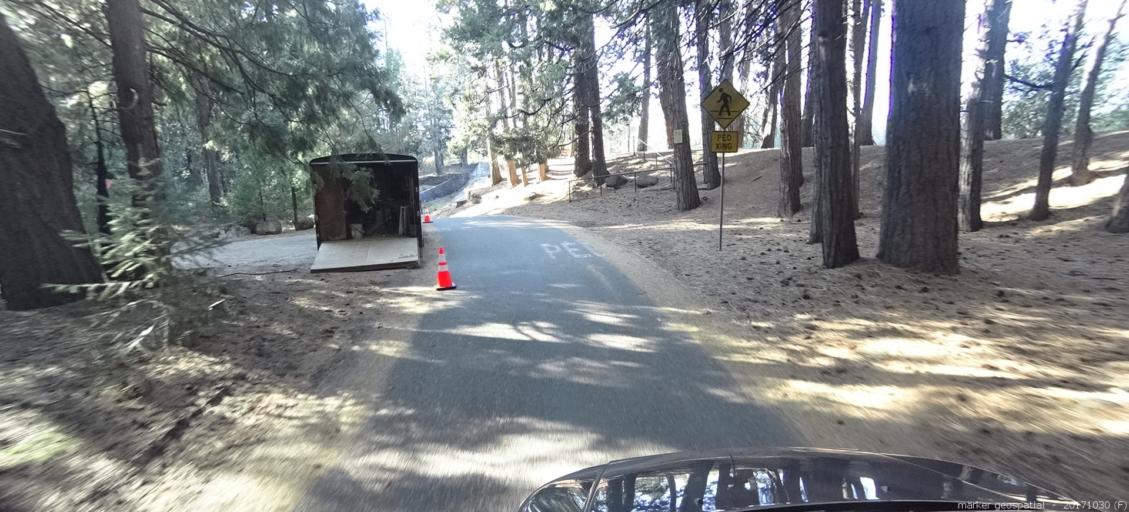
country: US
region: California
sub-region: Shasta County
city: Shingletown
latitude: 40.5376
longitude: -121.7317
